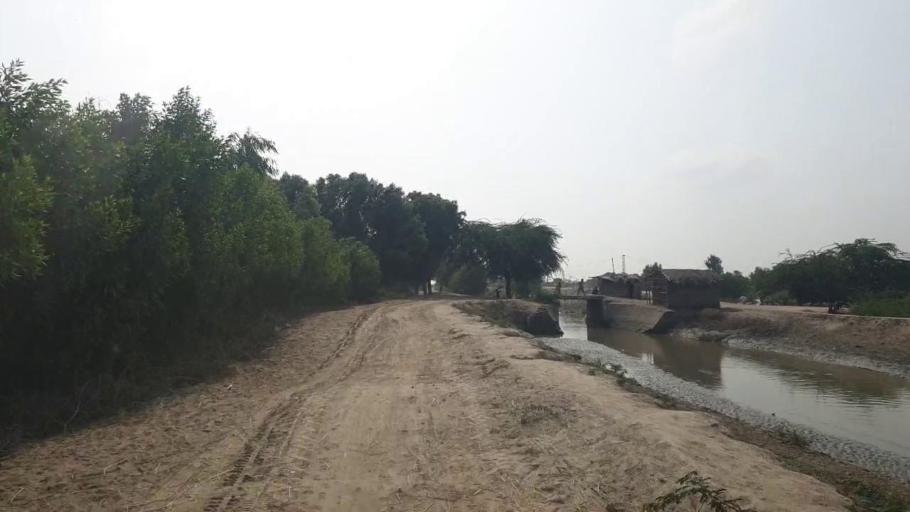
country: PK
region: Sindh
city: Badin
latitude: 24.5999
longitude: 68.7184
